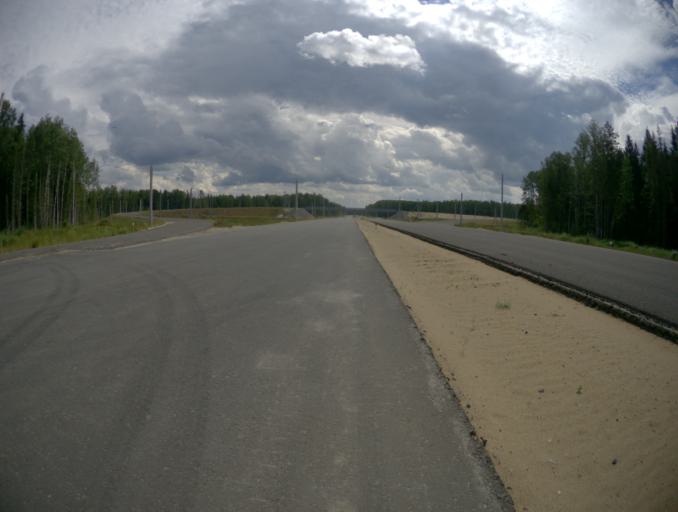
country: RU
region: Vladimir
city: Golovino
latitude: 56.0167
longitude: 40.5724
